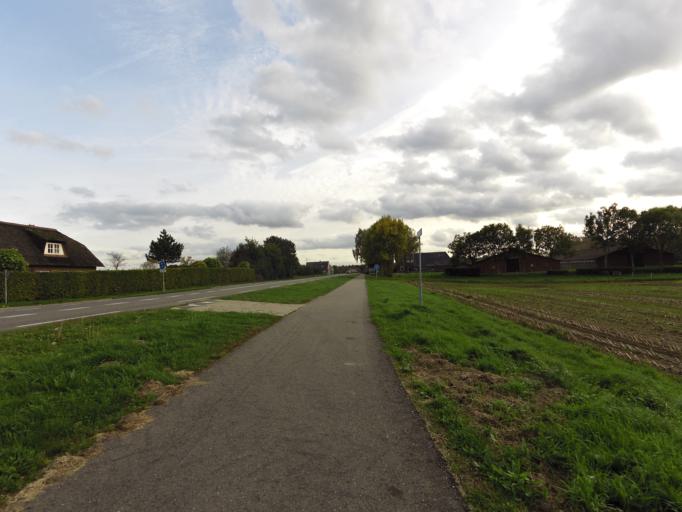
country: NL
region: Gelderland
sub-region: Gemeente Bronckhorst
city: Baak
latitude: 52.0830
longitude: 6.2235
